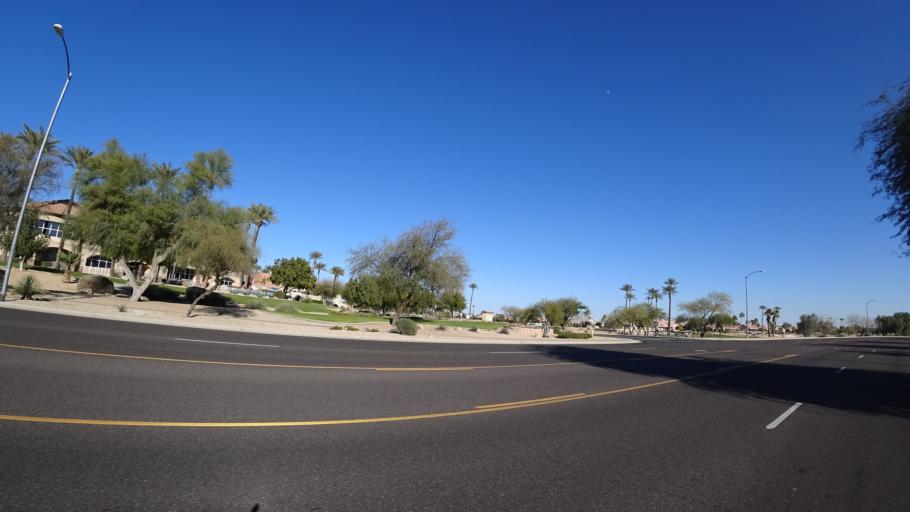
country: US
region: Arizona
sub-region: Maricopa County
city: Sun City West
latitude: 33.6865
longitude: -112.3582
